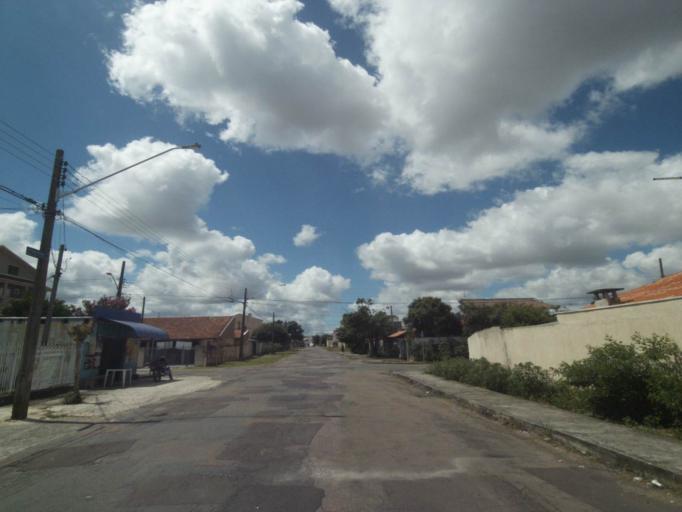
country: BR
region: Parana
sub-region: Pinhais
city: Pinhais
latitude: -25.4405
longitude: -49.2040
